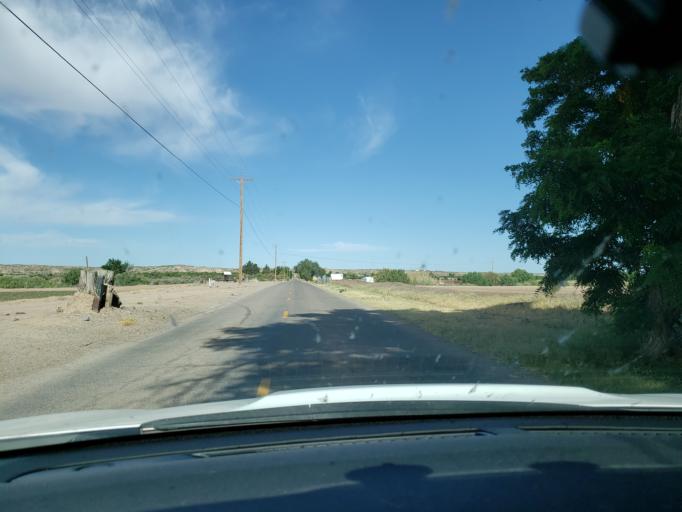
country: US
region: New Mexico
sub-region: Dona Ana County
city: Vado
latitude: 32.0826
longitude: -106.6910
